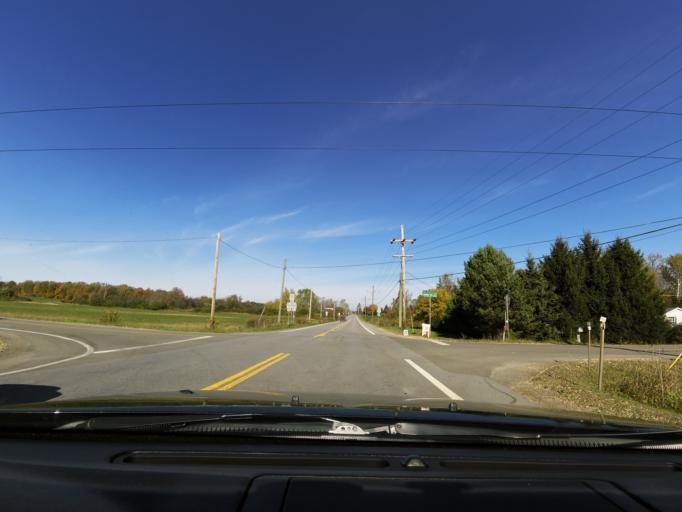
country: US
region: New York
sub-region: Wyoming County
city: Castile
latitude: 42.5910
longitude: -78.0686
